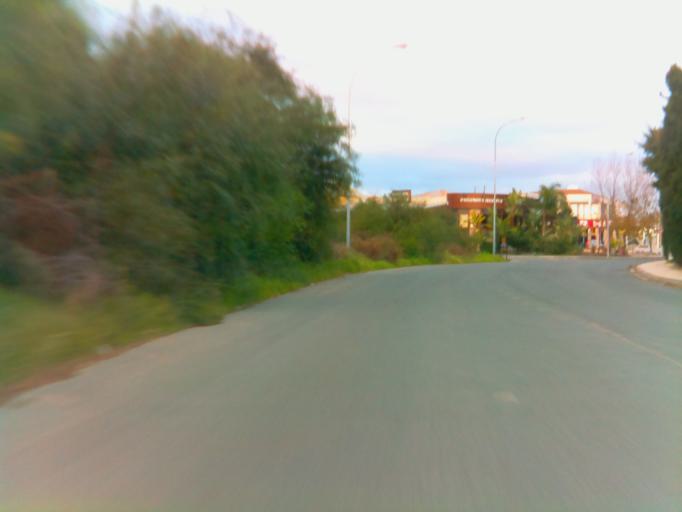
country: CY
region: Pafos
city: Pegeia
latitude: 34.8589
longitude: 32.3625
